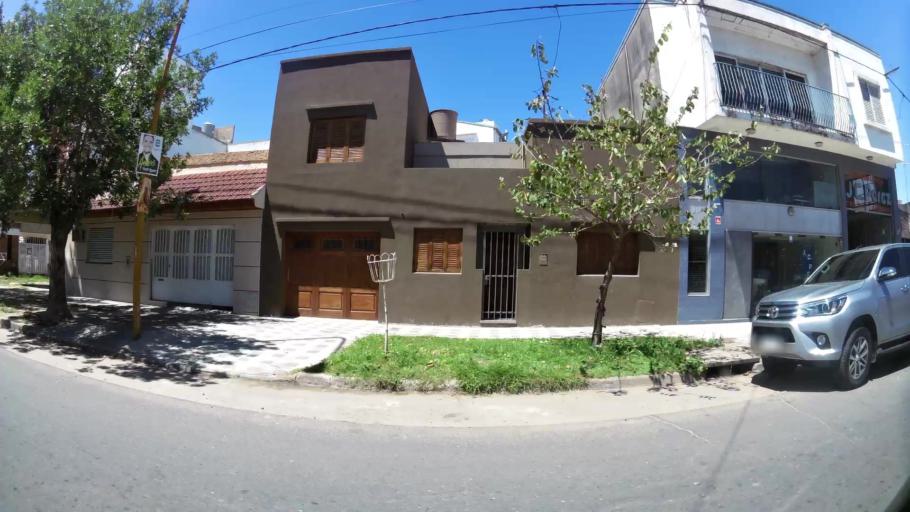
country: AR
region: Santa Fe
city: Santa Fe de la Vera Cruz
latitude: -31.6157
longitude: -60.7096
